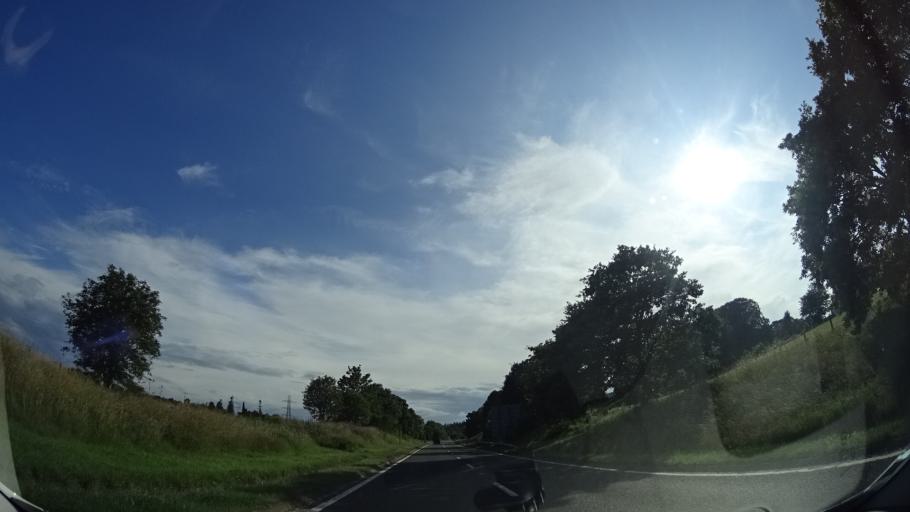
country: GB
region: Scotland
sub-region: Highland
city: Conon Bridge
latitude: 57.5774
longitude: -4.4471
